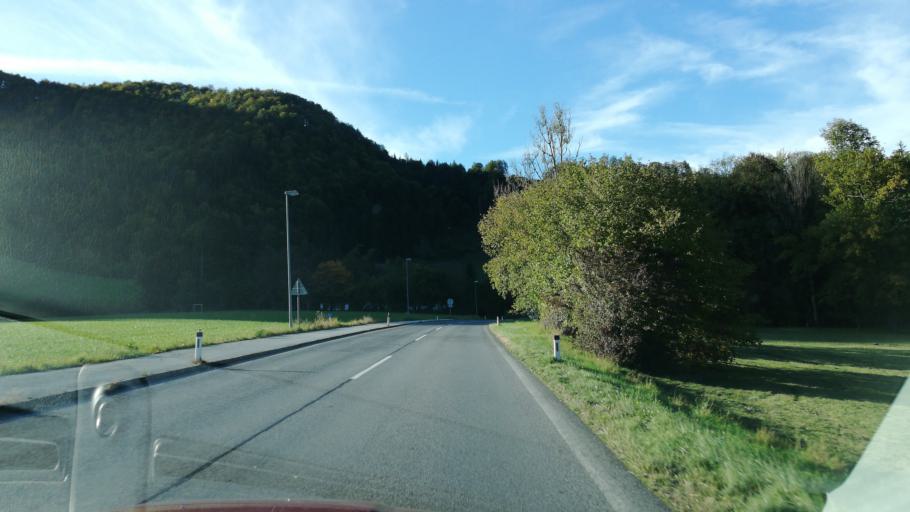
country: AT
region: Styria
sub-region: Politischer Bezirk Liezen
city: Landl
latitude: 47.6582
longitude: 14.7310
